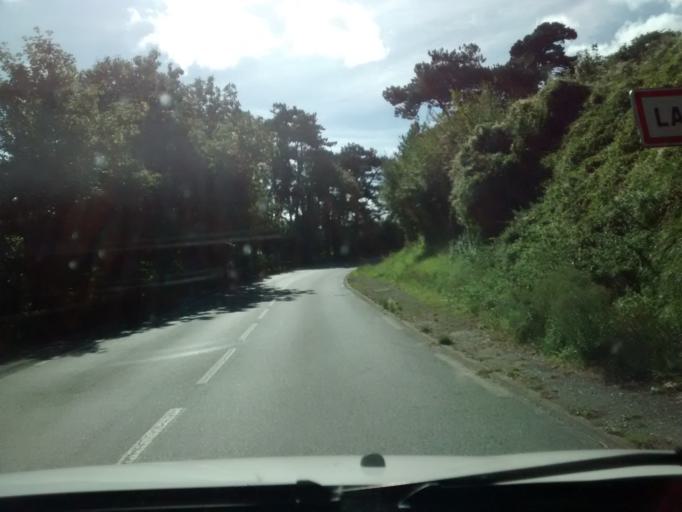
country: FR
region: Brittany
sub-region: Departement d'Ille-et-Vilaine
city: La Richardais
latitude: 48.6097
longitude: -2.0341
